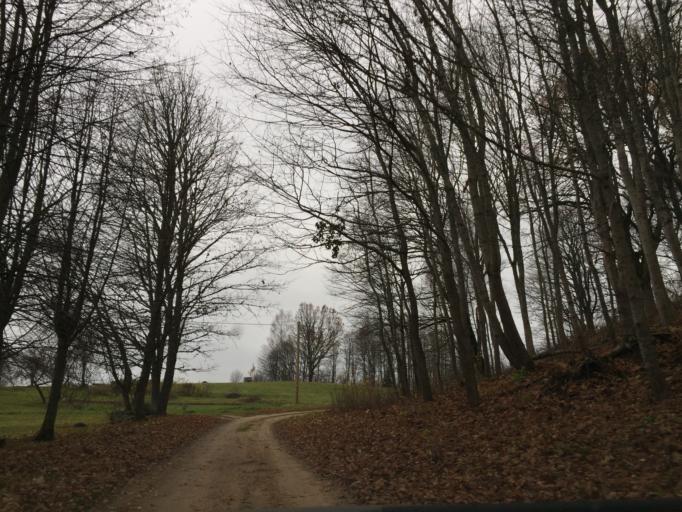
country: LV
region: Pargaujas
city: Stalbe
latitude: 57.5147
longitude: 25.0111
